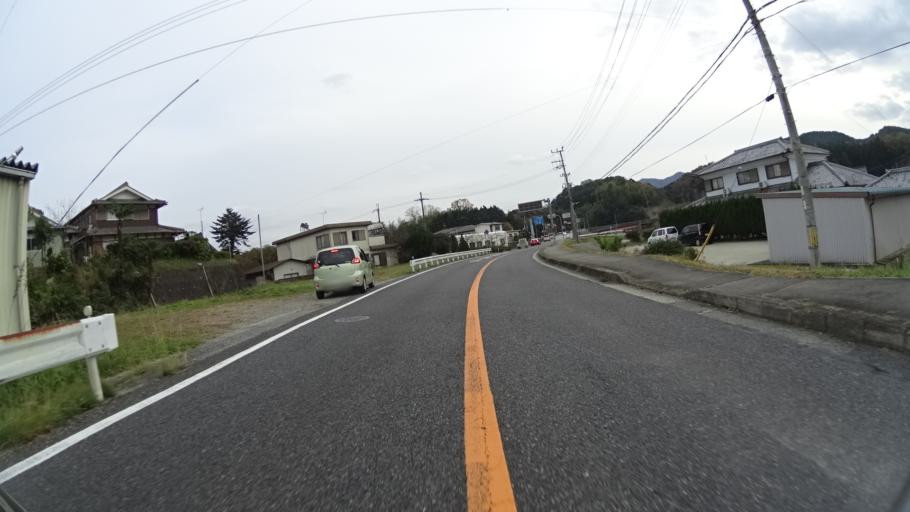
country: JP
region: Hyogo
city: Sasayama
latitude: 35.0785
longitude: 135.1657
